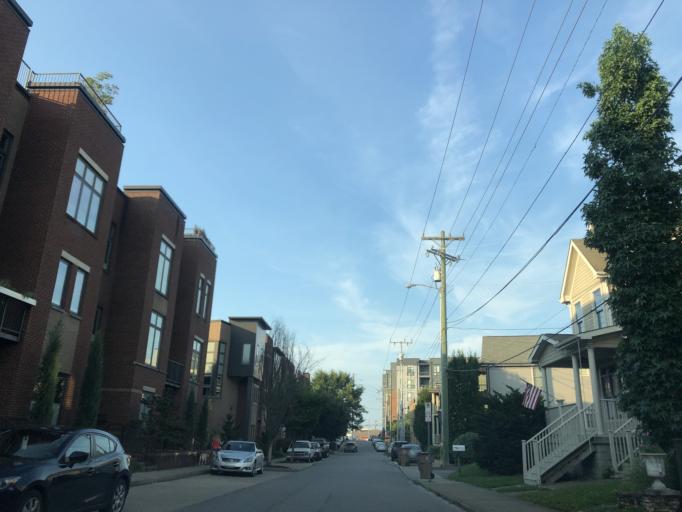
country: US
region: Tennessee
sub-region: Davidson County
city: Nashville
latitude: 36.1792
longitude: -86.7903
